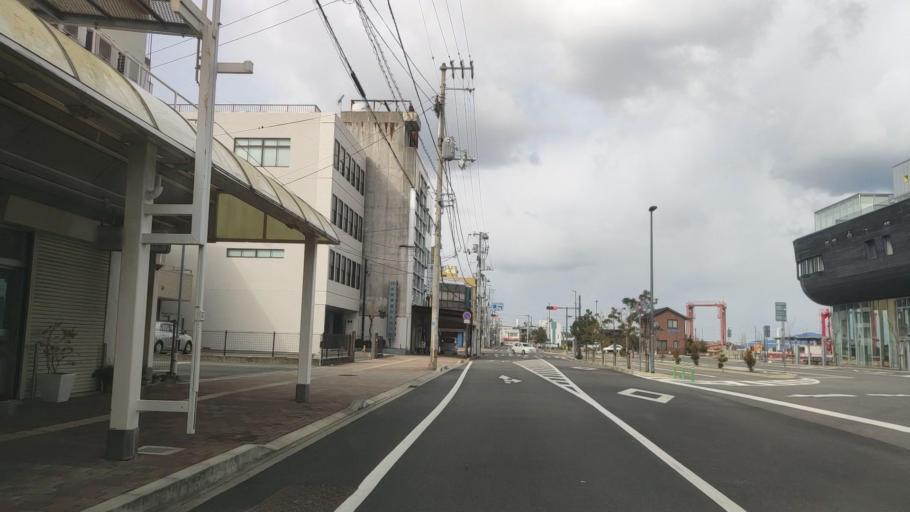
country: JP
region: Ehime
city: Saijo
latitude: 34.0694
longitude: 133.0050
